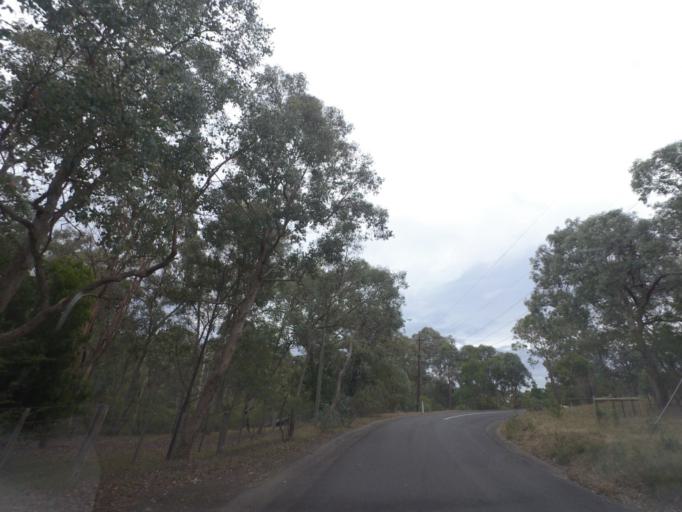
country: AU
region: Victoria
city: Plenty
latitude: -37.6608
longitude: 145.1328
